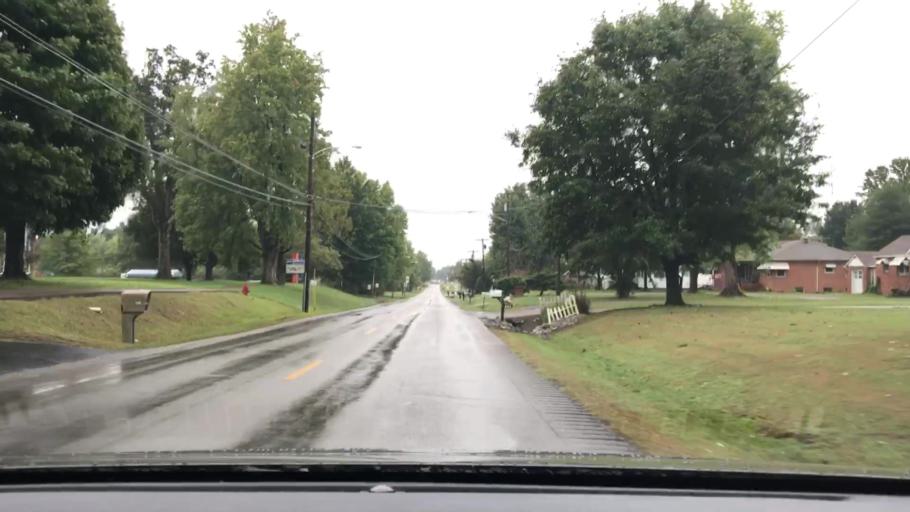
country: US
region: Kentucky
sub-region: McLean County
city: Calhoun
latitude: 37.4121
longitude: -87.2646
